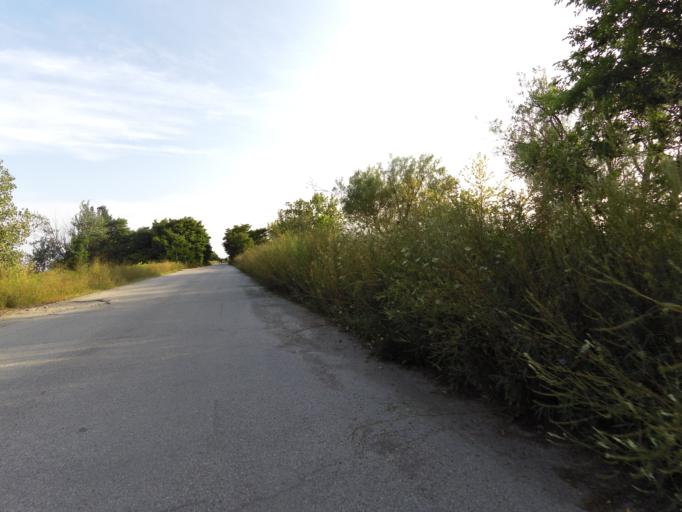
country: CA
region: Ontario
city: Toronto
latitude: 43.6442
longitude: -79.3214
